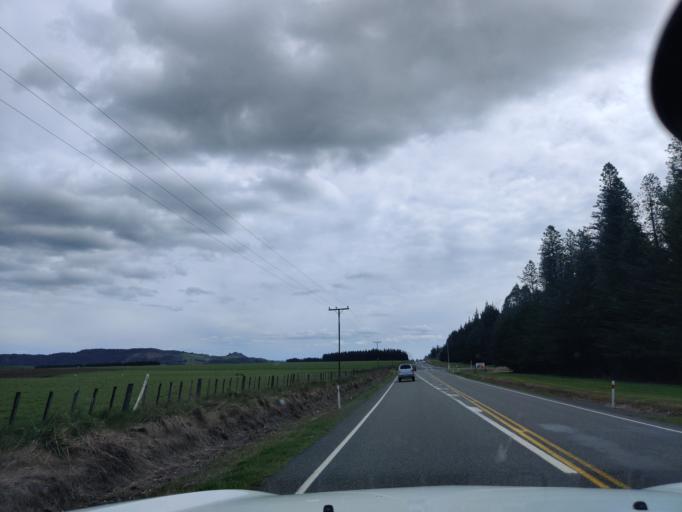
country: NZ
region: Manawatu-Wanganui
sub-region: Ruapehu District
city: Waiouru
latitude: -39.4687
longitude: 175.5678
